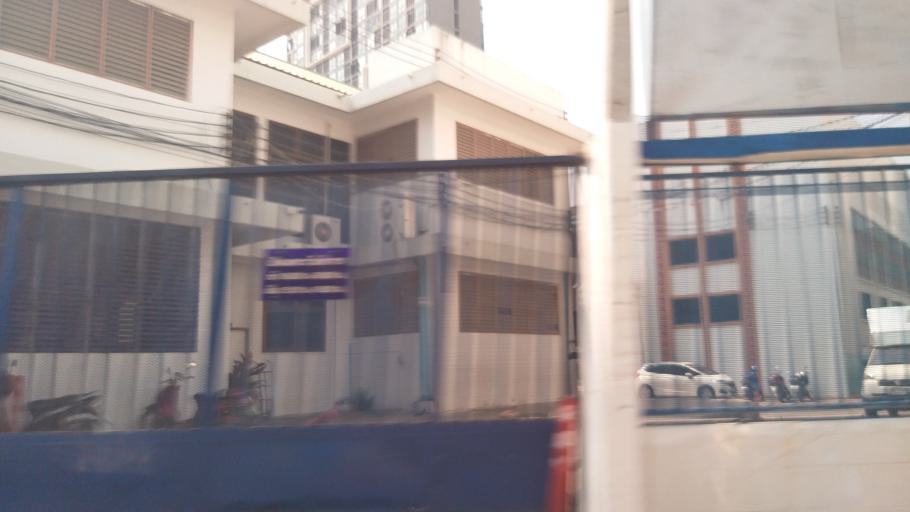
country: TH
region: Khon Kaen
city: Khon Kaen
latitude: 16.4328
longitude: 102.8323
